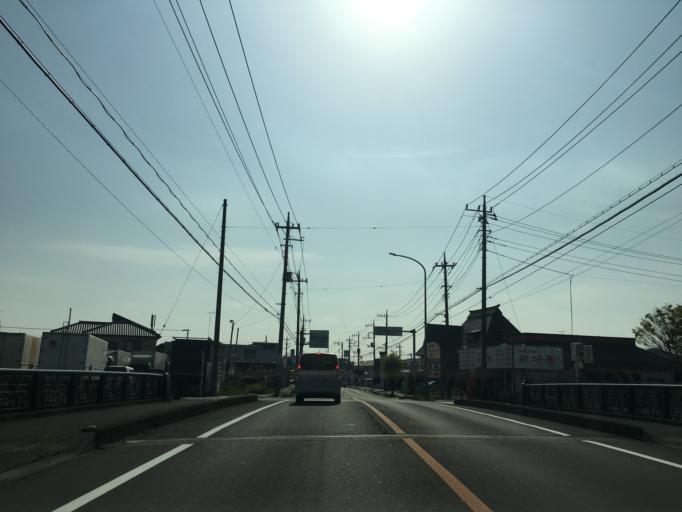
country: JP
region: Saitama
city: Ageoshimo
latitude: 35.9736
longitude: 139.6075
